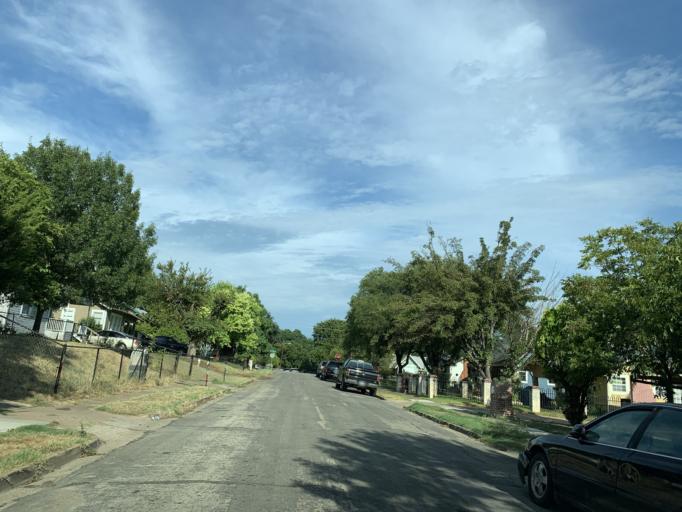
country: US
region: Texas
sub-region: Dallas County
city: Dallas
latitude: 32.7363
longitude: -96.8331
